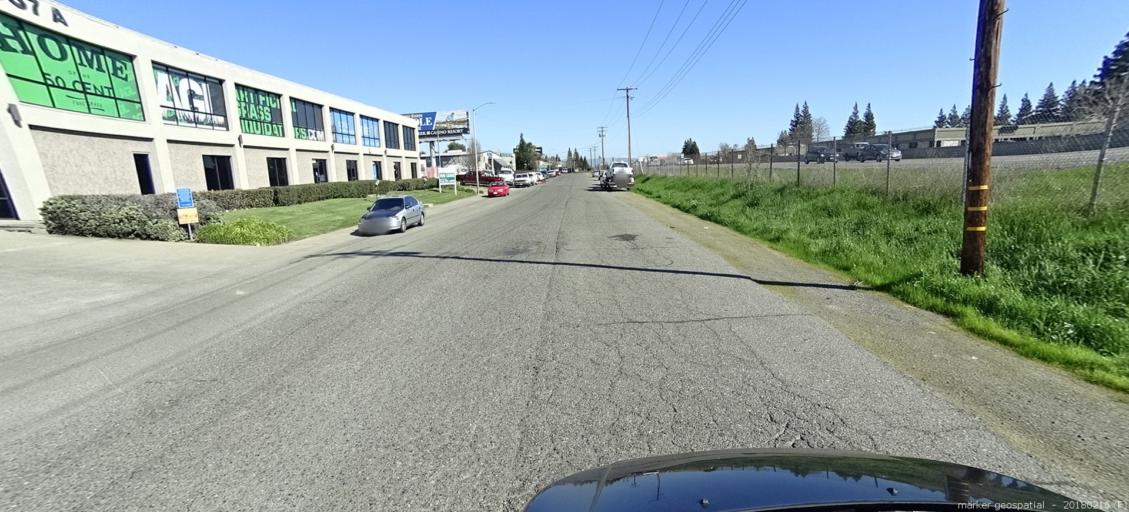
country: US
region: California
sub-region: Sacramento County
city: Gold River
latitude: 38.6146
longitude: -121.2564
